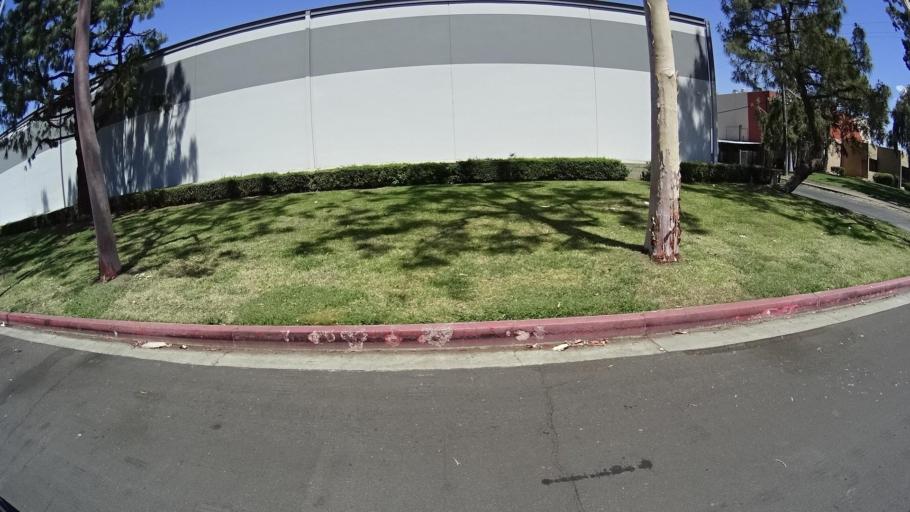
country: US
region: California
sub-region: Los Angeles County
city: La Puente
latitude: 34.0026
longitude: -117.9354
